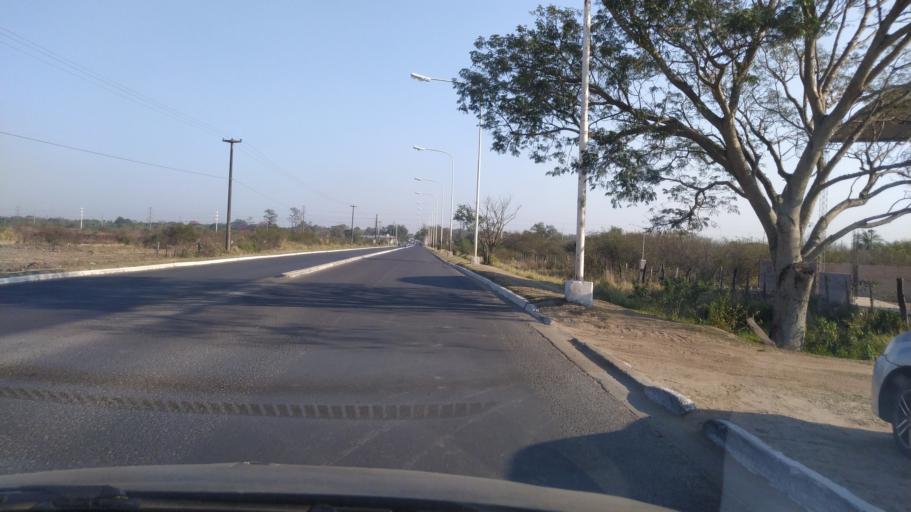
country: AR
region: Corrientes
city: Corrientes
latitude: -27.5186
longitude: -58.8019
